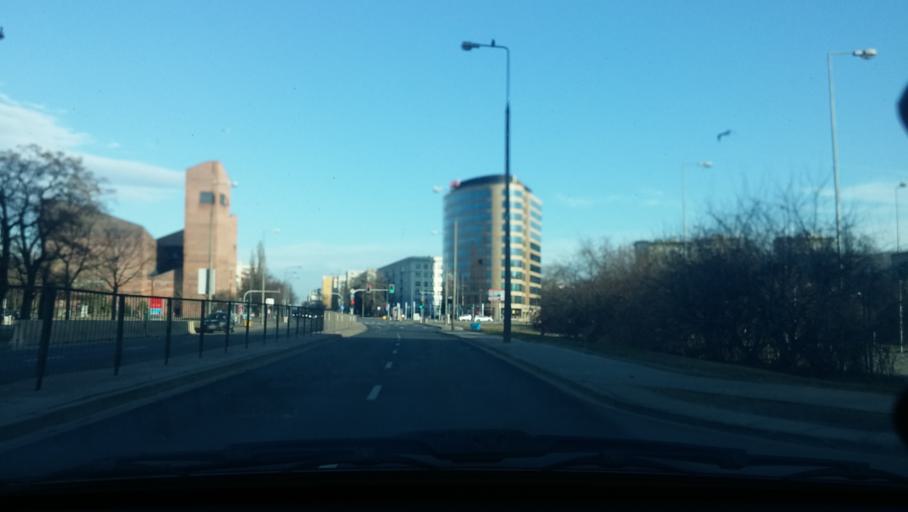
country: PL
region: Masovian Voivodeship
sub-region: Warszawa
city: Mokotow
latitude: 52.1819
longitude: 21.0209
